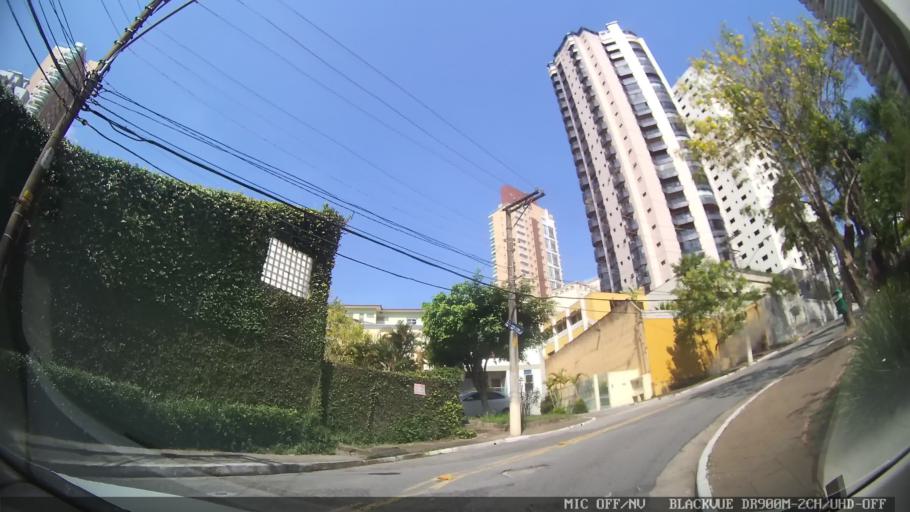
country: BR
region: Sao Paulo
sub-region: Sao Paulo
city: Sao Paulo
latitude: -23.4891
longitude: -46.6300
